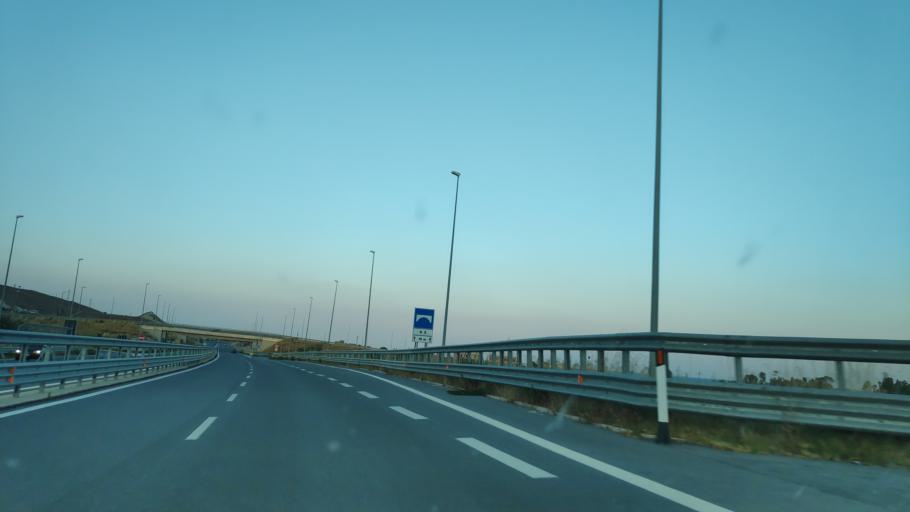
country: IT
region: Calabria
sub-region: Provincia di Reggio Calabria
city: Marina di Gioiosa Ionica
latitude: 38.3102
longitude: 16.3499
